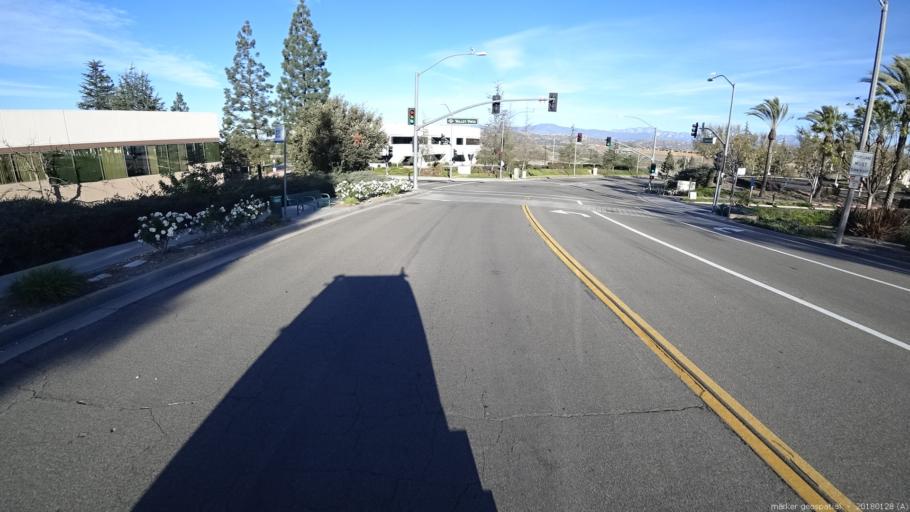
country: US
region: California
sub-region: Los Angeles County
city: Walnut
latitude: 33.9984
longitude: -117.8357
